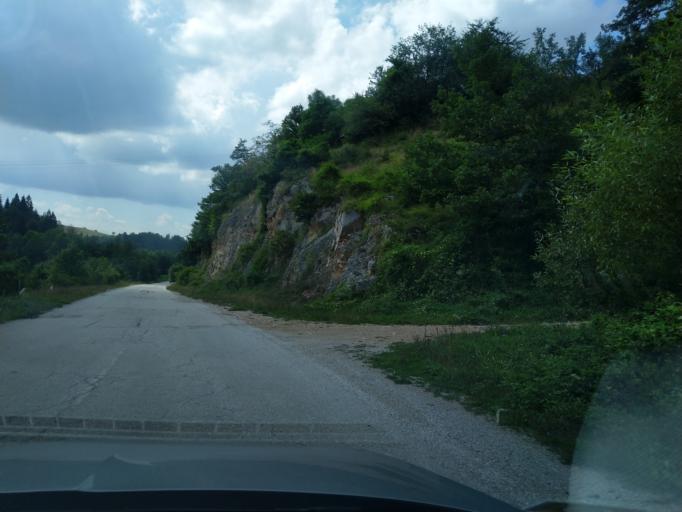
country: RS
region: Central Serbia
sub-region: Zlatiborski Okrug
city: Nova Varos
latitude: 43.5398
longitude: 19.9074
